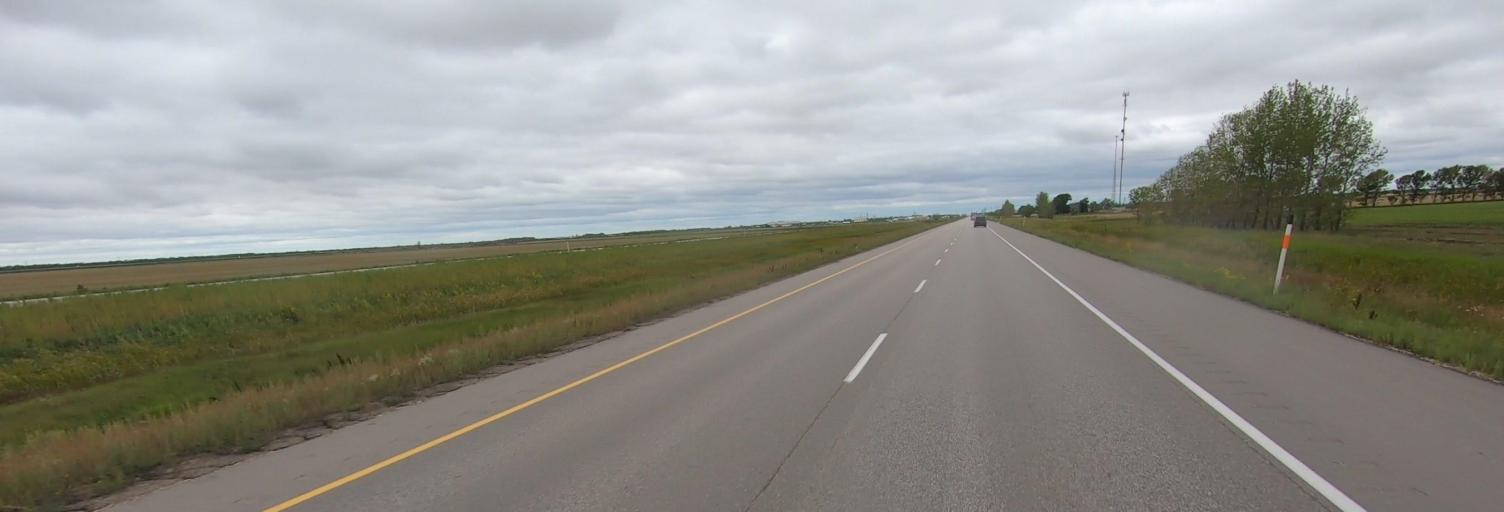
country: CA
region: Manitoba
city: Headingley
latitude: 49.8969
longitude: -97.7032
